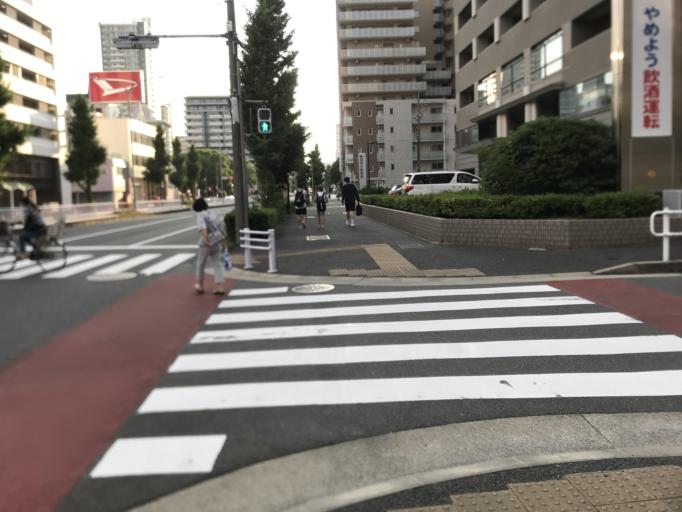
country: JP
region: Aichi
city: Nagoya-shi
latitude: 35.1567
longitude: 136.9118
